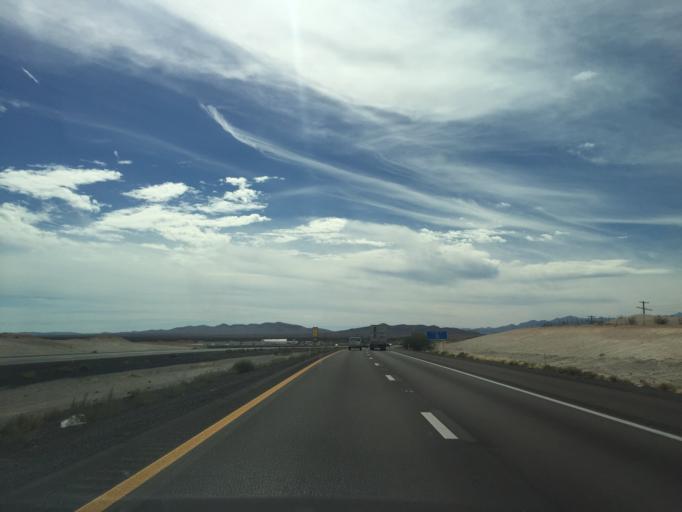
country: US
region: Nevada
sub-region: Clark County
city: Moapa Town
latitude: 36.5086
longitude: -114.7513
